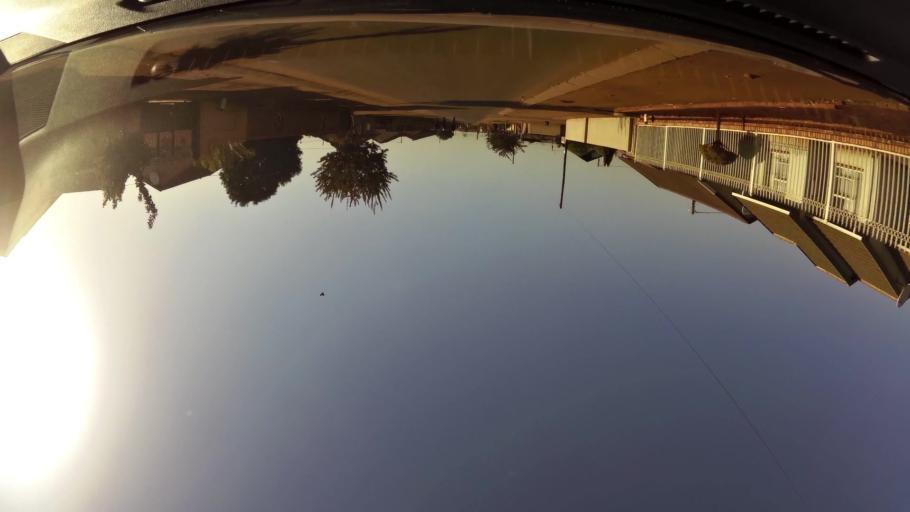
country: ZA
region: Gauteng
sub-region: City of Tshwane Metropolitan Municipality
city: Mabopane
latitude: -25.5887
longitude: 28.0976
